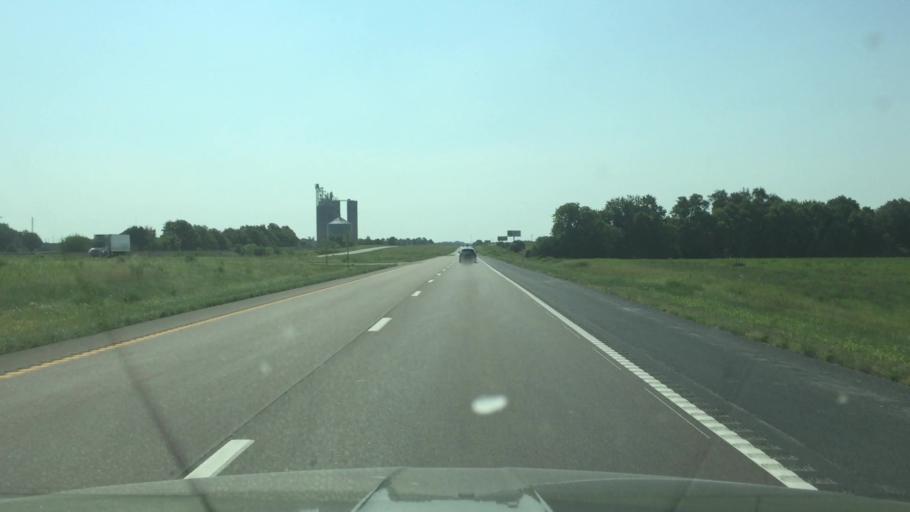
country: US
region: Missouri
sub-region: Pettis County
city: La Monte
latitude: 38.7535
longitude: -93.3566
